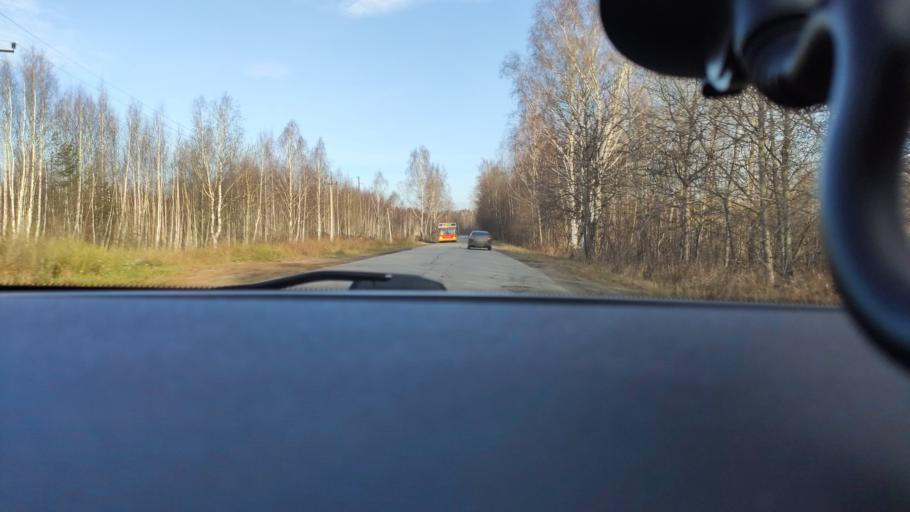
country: RU
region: Perm
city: Kondratovo
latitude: 58.0556
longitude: 56.0280
